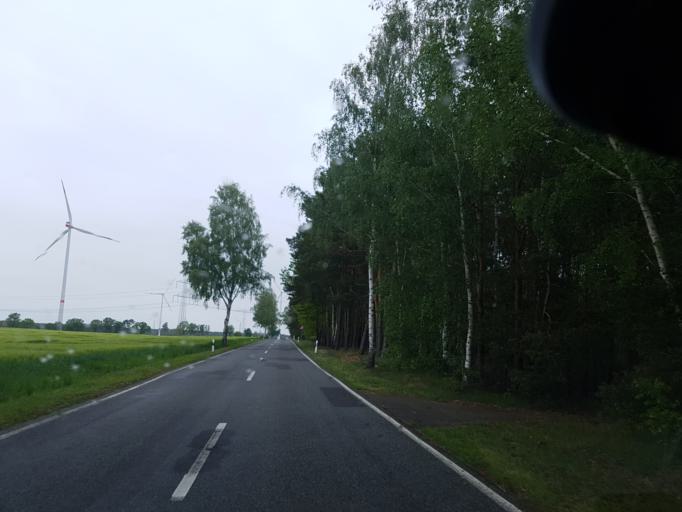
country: DE
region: Brandenburg
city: Drebkau
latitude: 51.6460
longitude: 14.2784
